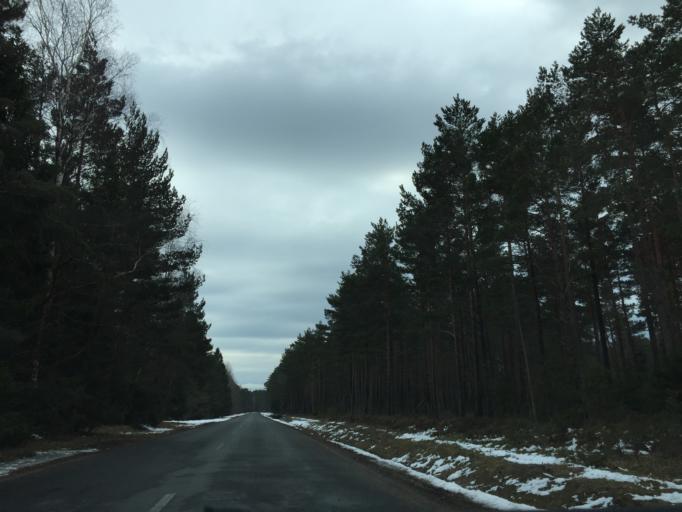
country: EE
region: Saare
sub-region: Kuressaare linn
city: Kuressaare
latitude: 58.4232
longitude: 22.0740
